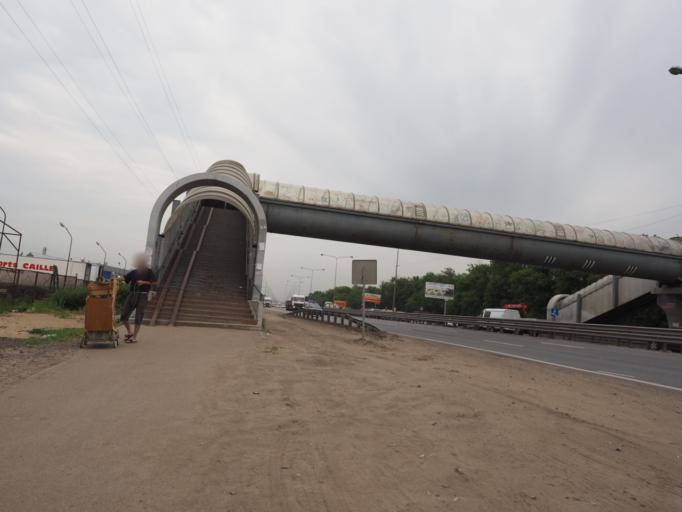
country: RU
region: Moskovskaya
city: Lyubertsy
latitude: 55.6560
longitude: 37.8998
